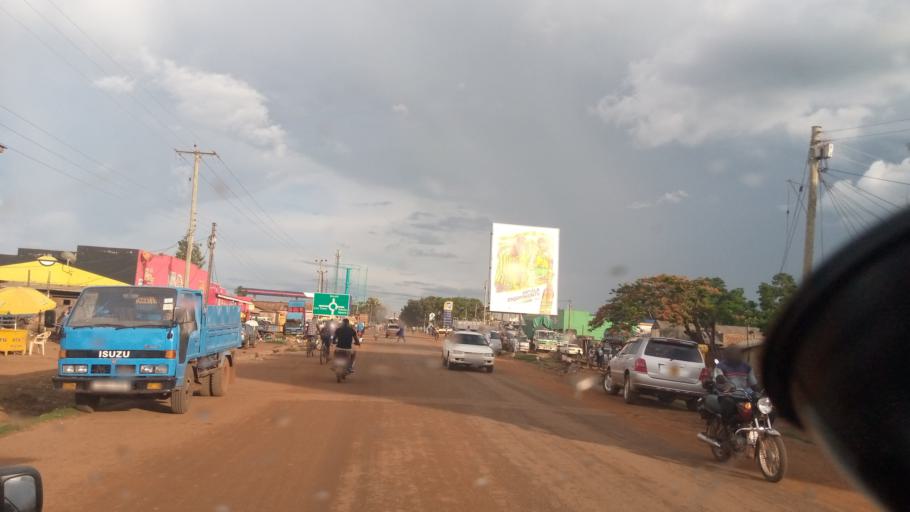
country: UG
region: Northern Region
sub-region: Lira District
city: Lira
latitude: 2.2374
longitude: 32.8907
